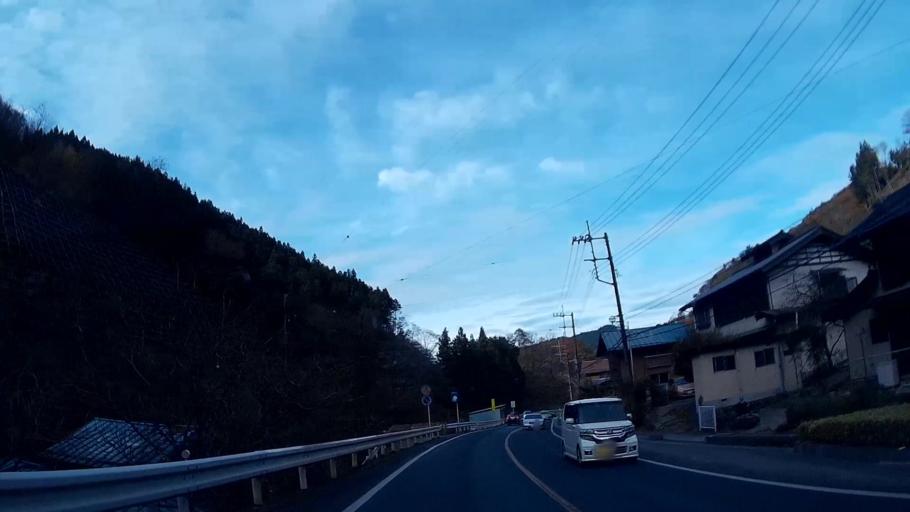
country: JP
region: Saitama
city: Chichibu
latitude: 35.9765
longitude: 139.1440
